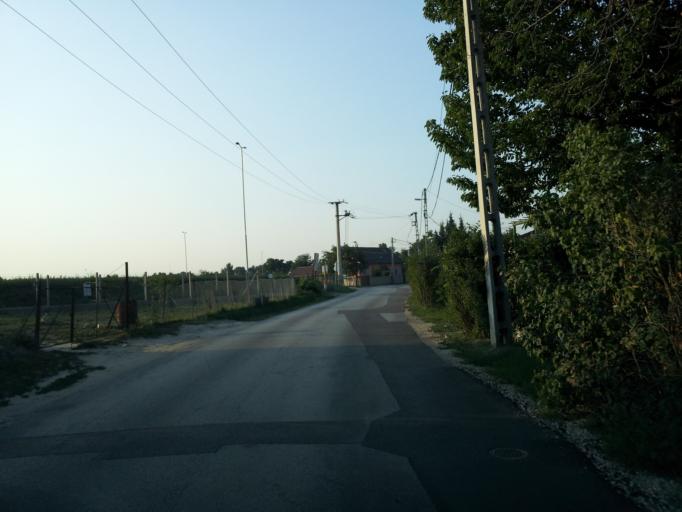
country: HU
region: Pest
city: Szigetszentmiklos
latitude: 47.3218
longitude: 19.0322
